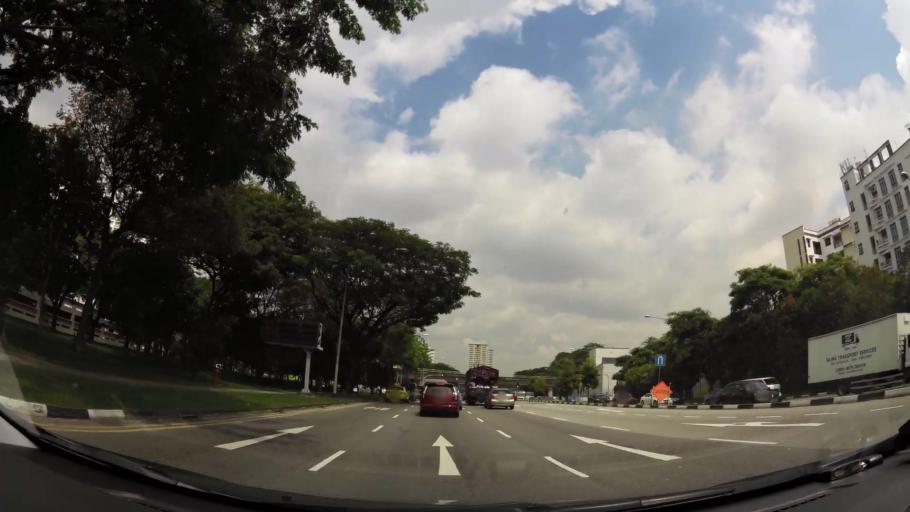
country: SG
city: Singapore
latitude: 1.3123
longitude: 103.8751
